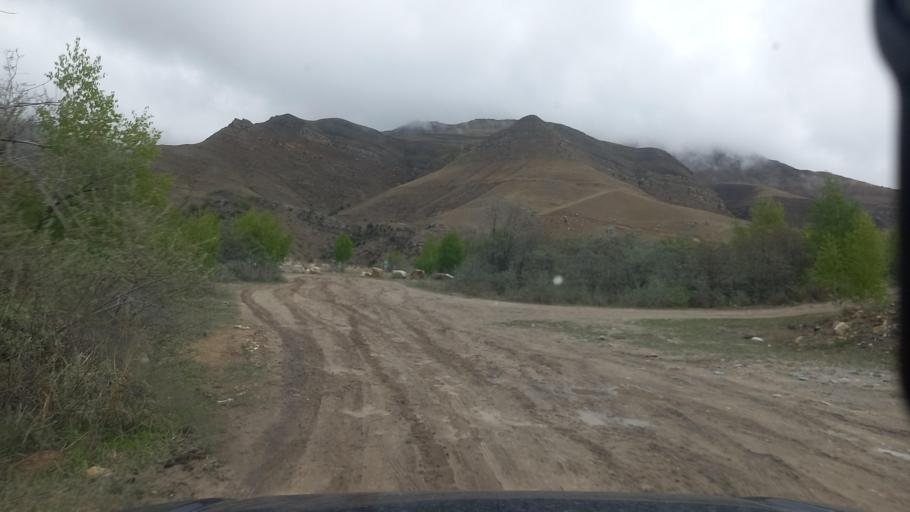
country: RU
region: Kabardino-Balkariya
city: Bylym
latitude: 43.4608
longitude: 42.9937
